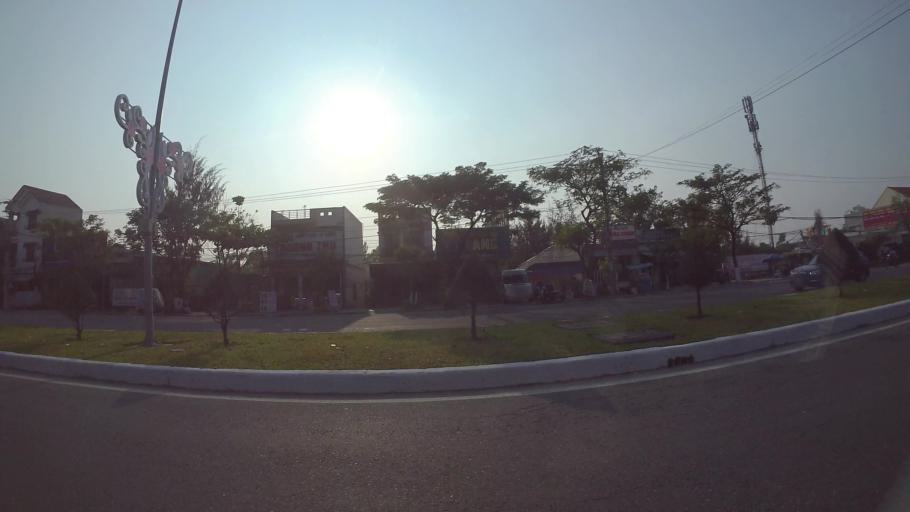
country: VN
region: Da Nang
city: Ngu Hanh Son
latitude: 15.9724
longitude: 108.2548
